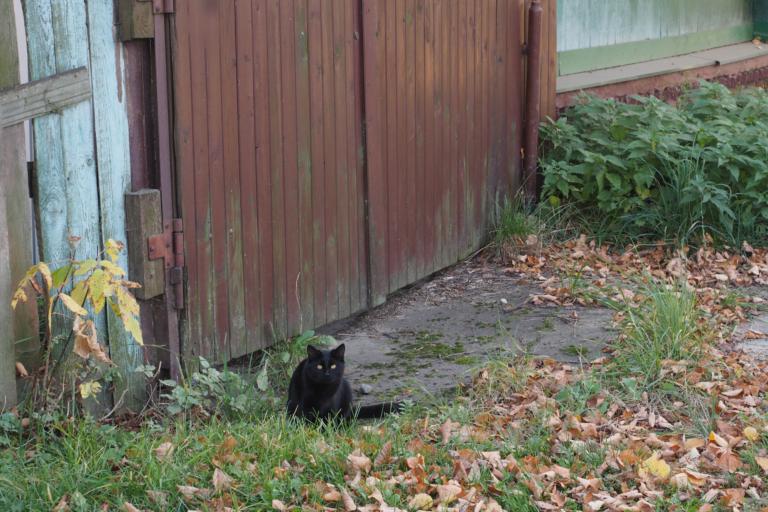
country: RU
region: Moskovskaya
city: Kurovskoye
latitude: 55.5779
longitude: 38.9057
